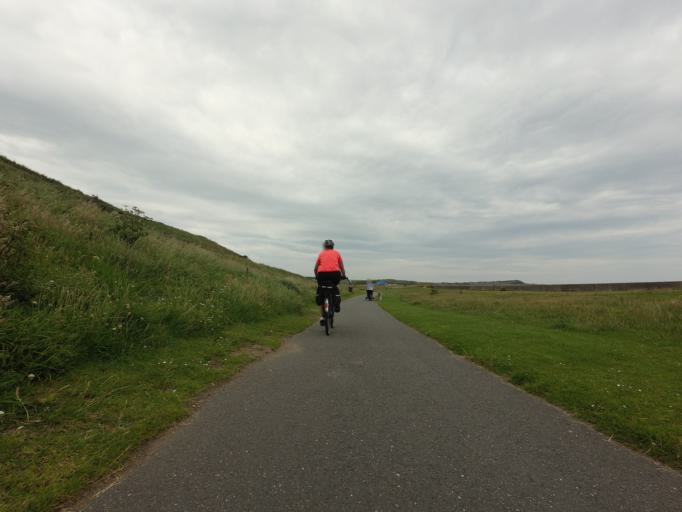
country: GB
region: Scotland
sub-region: Aberdeenshire
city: Banff
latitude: 57.6695
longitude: -2.5461
